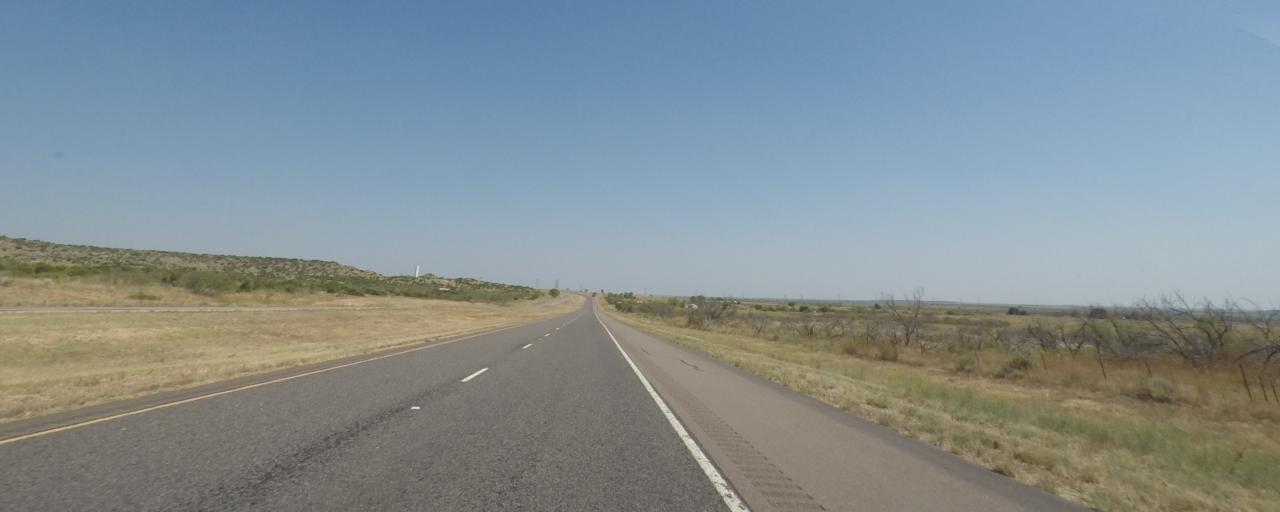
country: US
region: Texas
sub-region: Dickens County
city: Dickens
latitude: 33.6263
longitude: -100.8688
